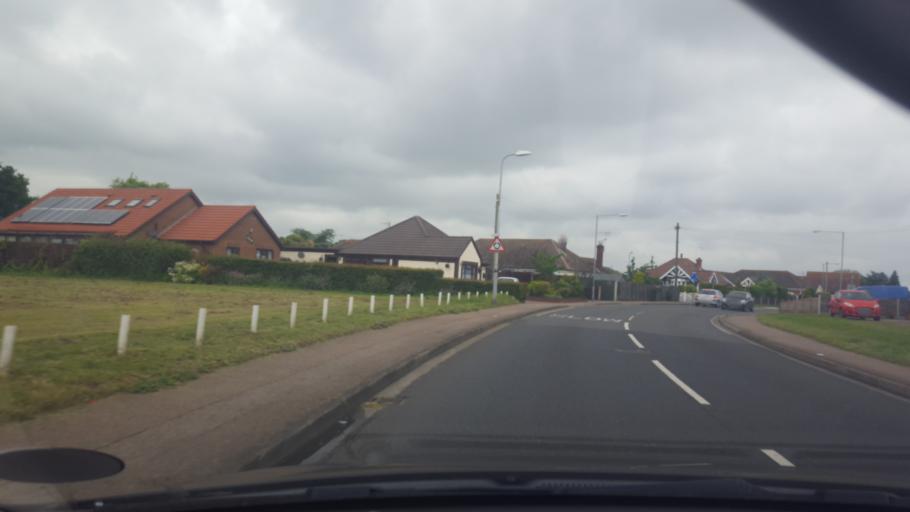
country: GB
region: England
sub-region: Essex
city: Clacton-on-Sea
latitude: 51.8094
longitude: 1.1663
